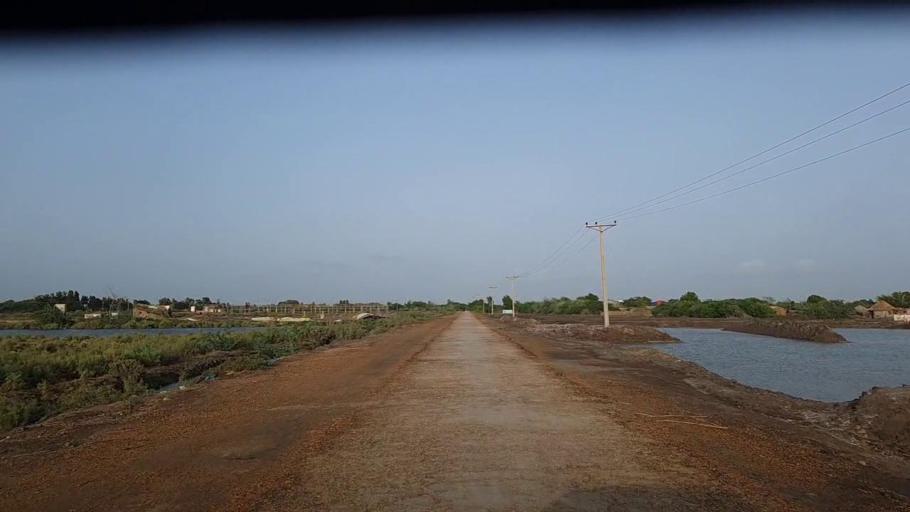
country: PK
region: Sindh
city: Thatta
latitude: 24.7600
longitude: 67.9108
